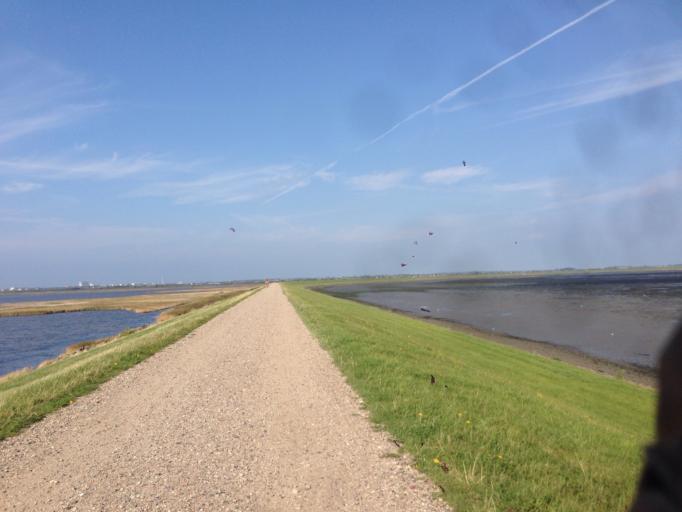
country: DE
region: Schleswig-Holstein
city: Tinnum
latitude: 54.8675
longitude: 8.3333
